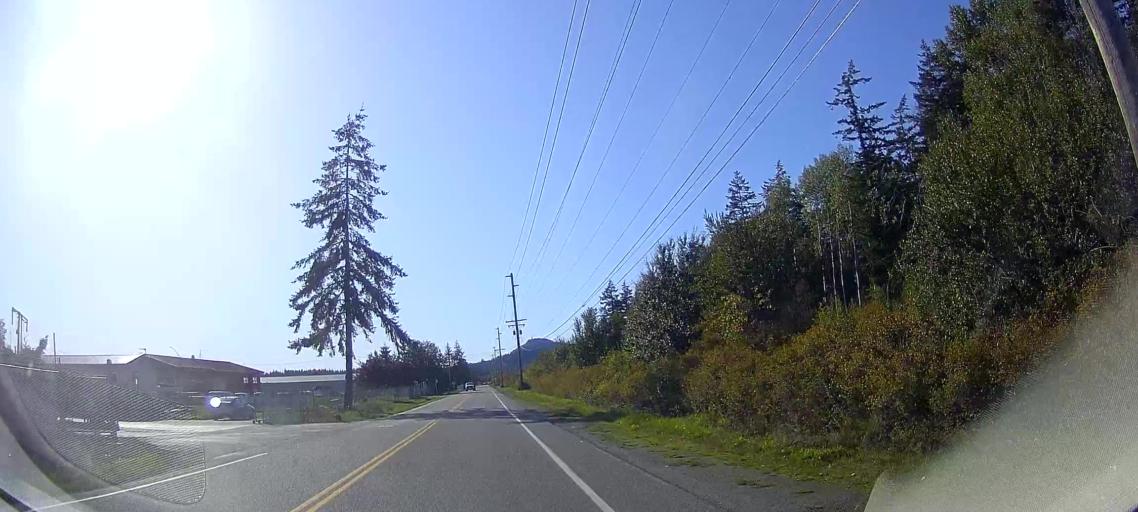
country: US
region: Washington
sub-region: Skagit County
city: Anacortes
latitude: 48.4632
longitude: -122.5508
